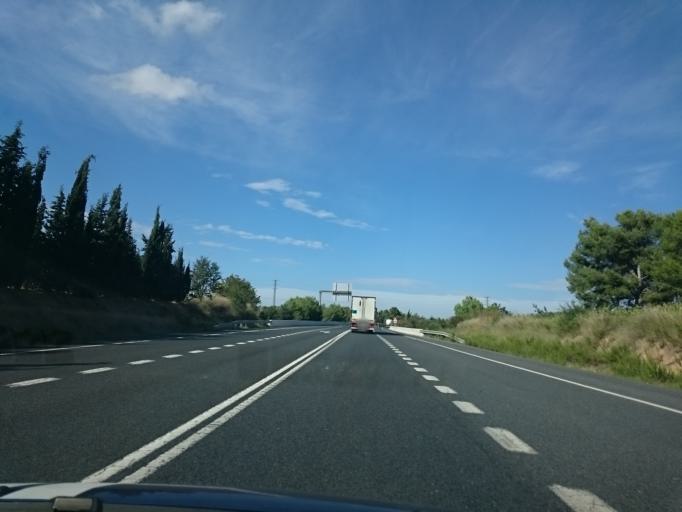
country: ES
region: Catalonia
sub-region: Provincia de Barcelona
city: Castellet
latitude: 41.3142
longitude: 1.6406
